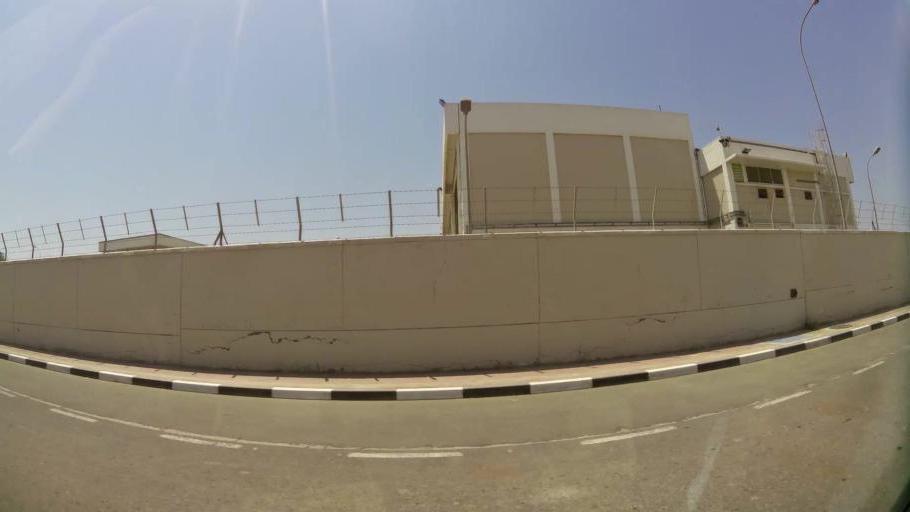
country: AE
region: Ash Shariqah
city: Sharjah
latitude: 25.2943
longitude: 55.3433
